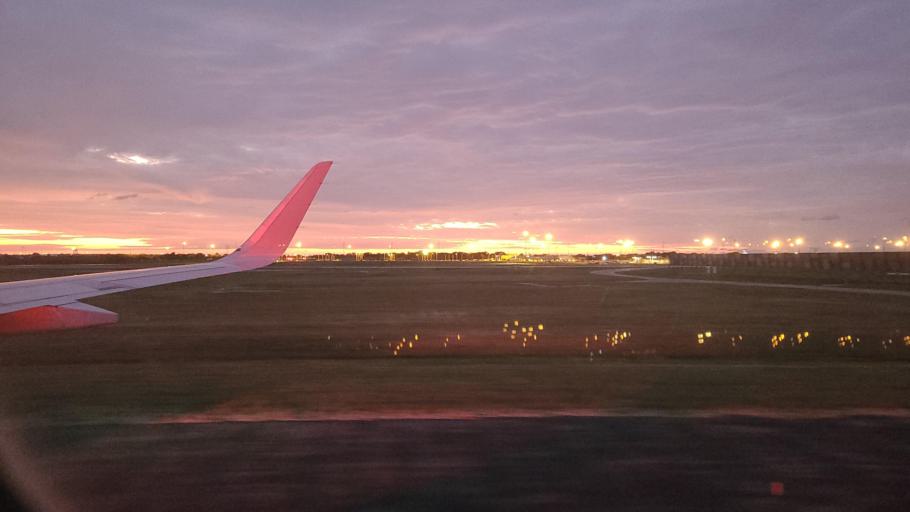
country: US
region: Texas
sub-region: Tarrant County
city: Euless
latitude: 32.8747
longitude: -97.0287
